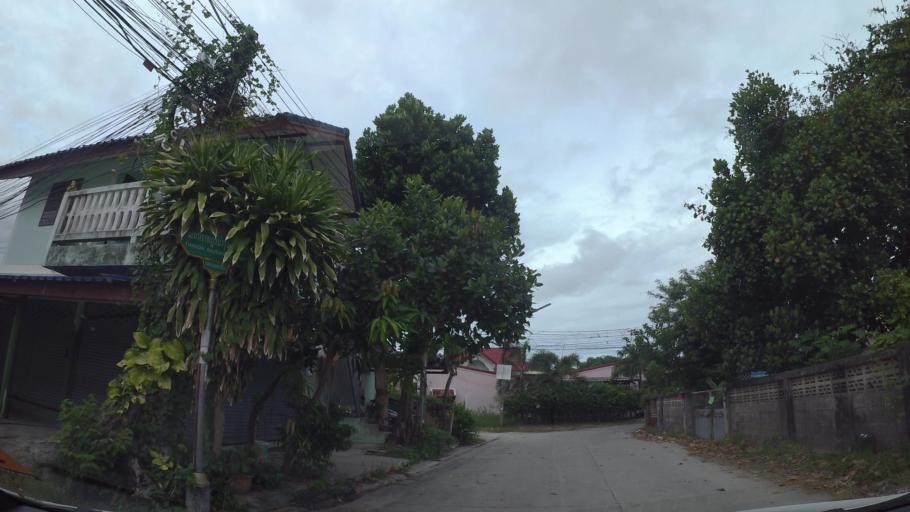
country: TH
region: Rayong
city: Rayong
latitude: 12.6760
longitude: 101.2669
